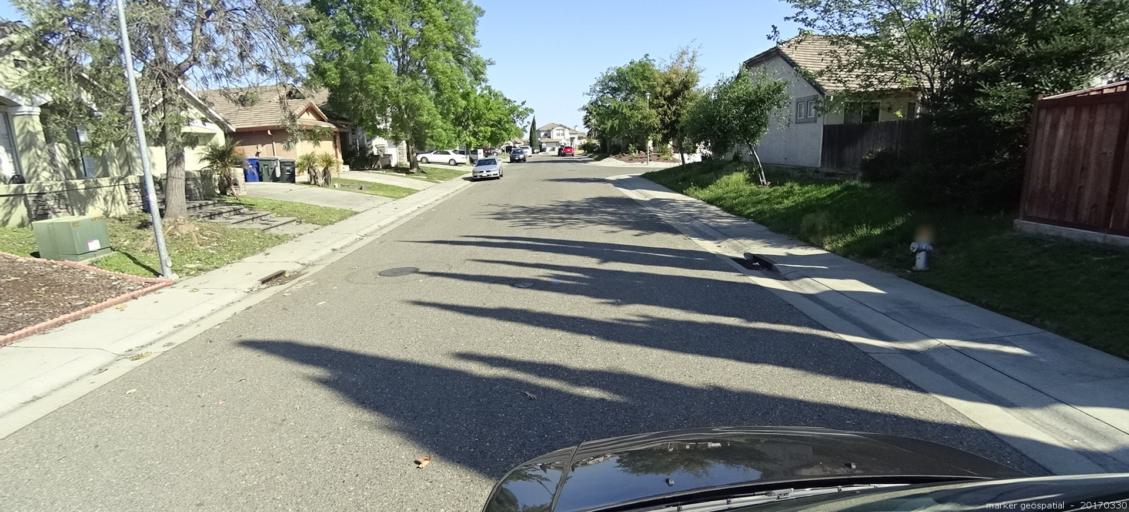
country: US
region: California
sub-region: Sacramento County
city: Laguna
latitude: 38.4474
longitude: -121.4121
